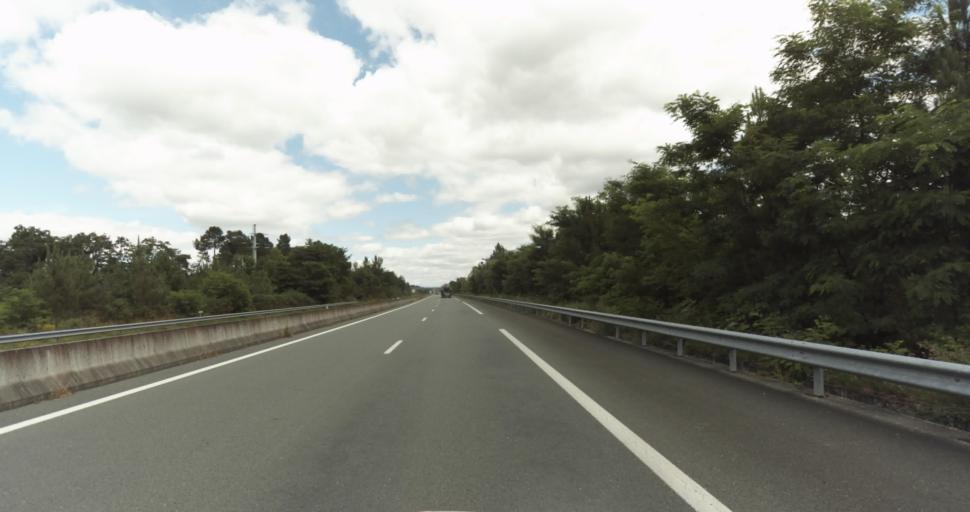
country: FR
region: Aquitaine
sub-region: Departement de la Gironde
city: Bazas
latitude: 44.4600
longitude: -0.2252
